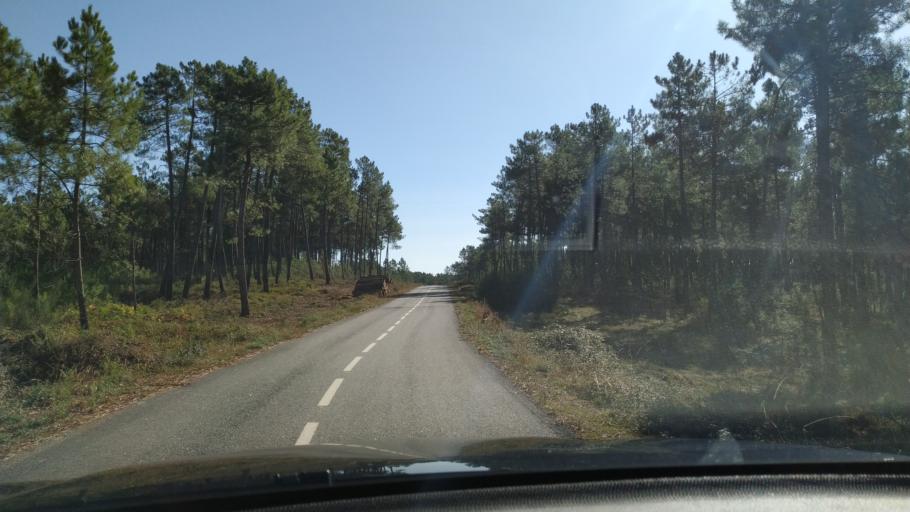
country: PT
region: Vila Real
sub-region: Sabrosa
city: Vilela
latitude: 41.2294
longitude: -7.6193
